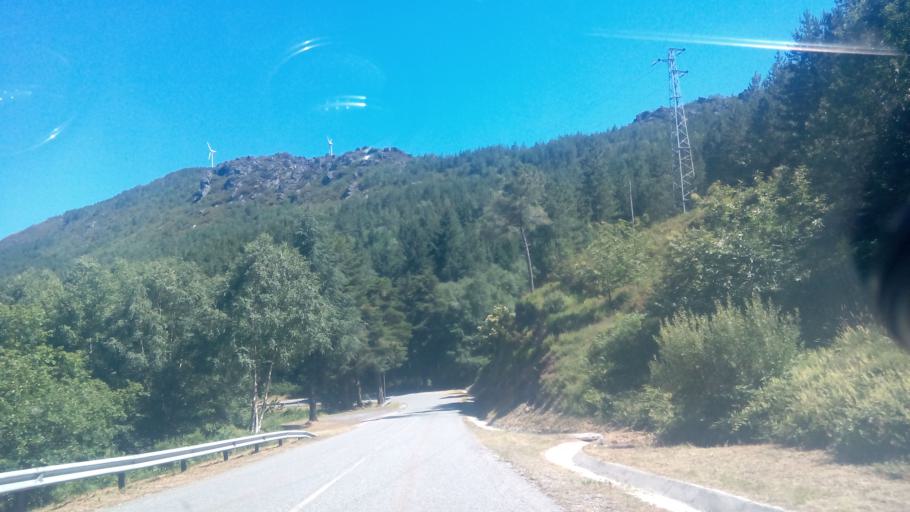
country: PT
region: Vila Real
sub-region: Mesao Frio
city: Mesao Frio
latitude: 41.2770
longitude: -7.9093
